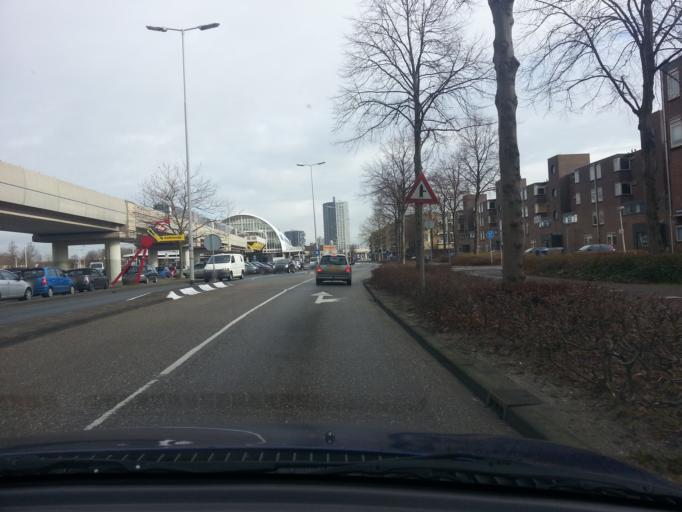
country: NL
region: South Holland
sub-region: Gemeente Spijkenisse
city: Spijkenisse
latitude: 51.8448
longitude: 4.3329
